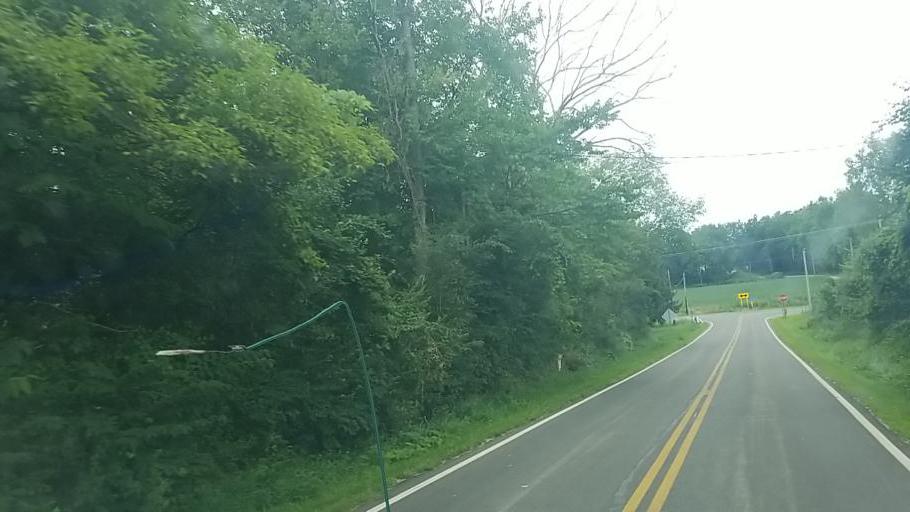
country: US
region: Ohio
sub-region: Medina County
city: Westfield Center
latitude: 41.0133
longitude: -81.9298
